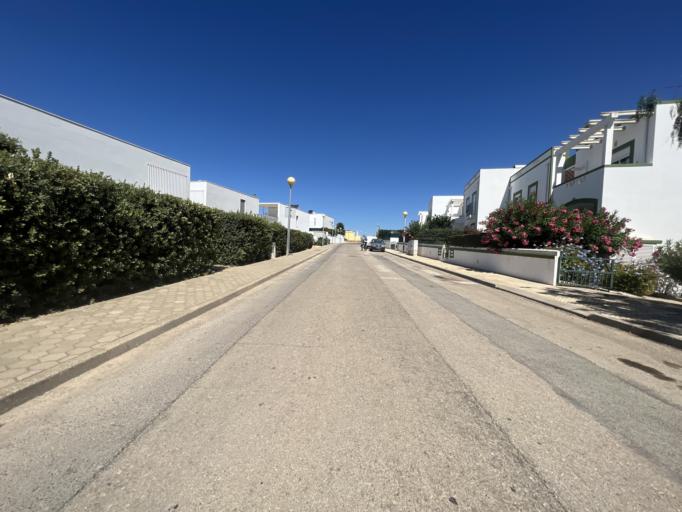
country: PT
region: Faro
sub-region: Portimao
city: Portimao
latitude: 37.1282
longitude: -8.5113
